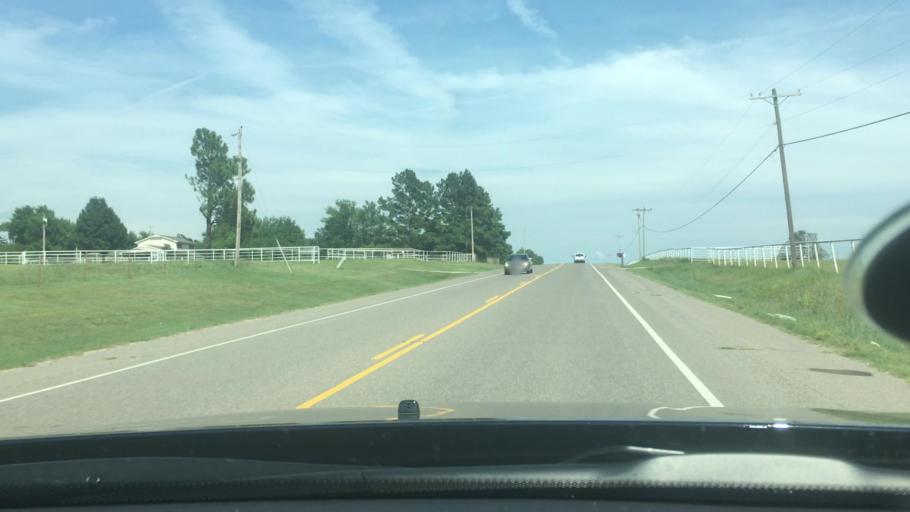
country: US
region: Oklahoma
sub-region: Pottawatomie County
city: Shawnee
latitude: 35.3331
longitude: -96.8241
